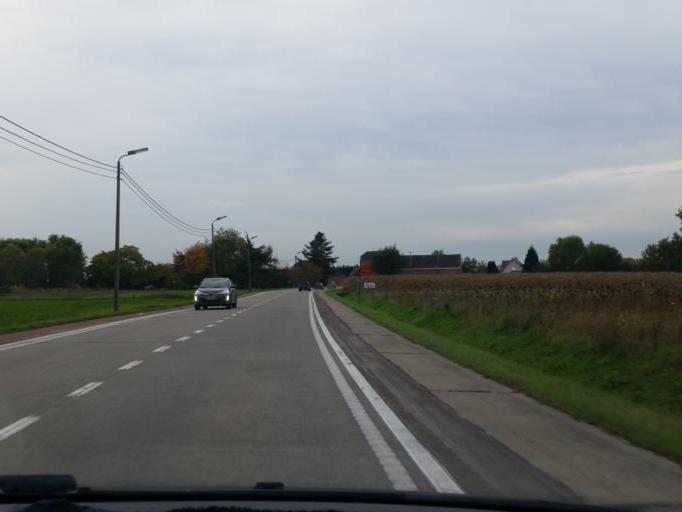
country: BE
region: Flanders
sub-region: Provincie Antwerpen
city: Sint-Katelijne-Waver
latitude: 51.0769
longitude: 4.5834
